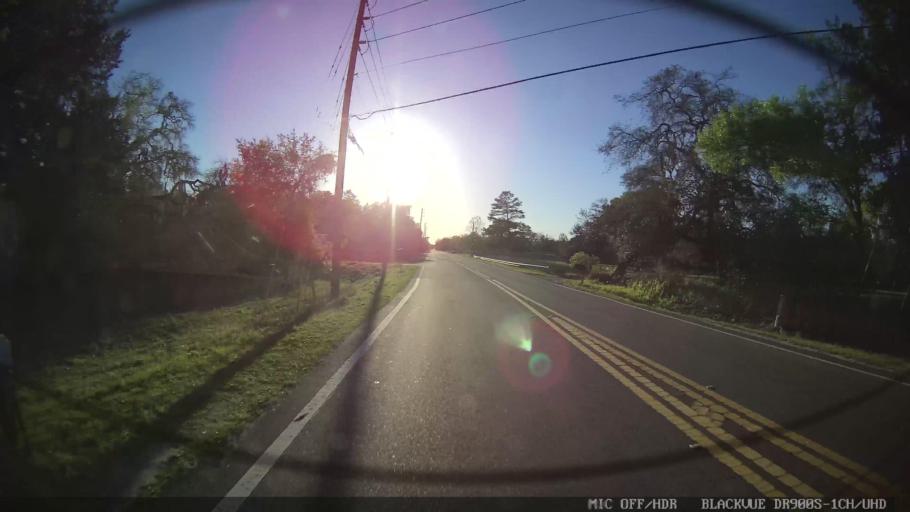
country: US
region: Florida
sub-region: Pasco County
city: Shady Hills
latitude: 28.3919
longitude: -82.5534
